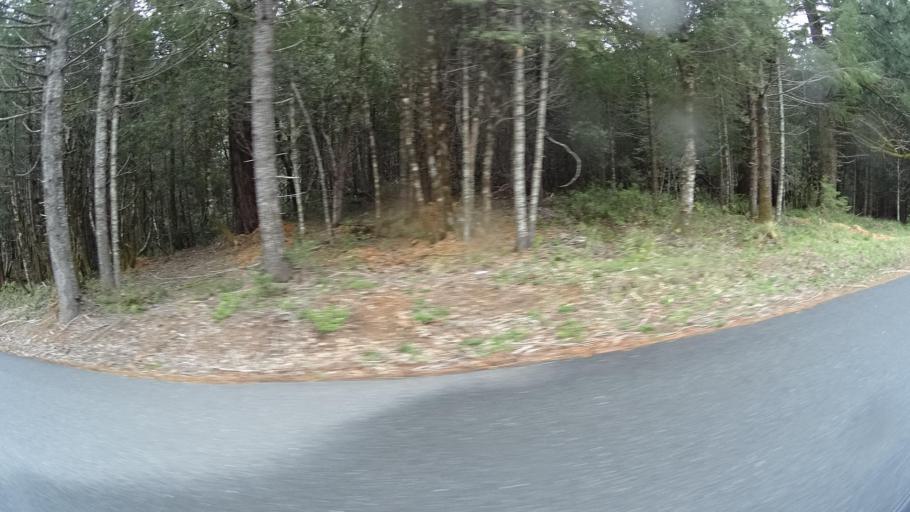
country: US
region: California
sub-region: Humboldt County
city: Willow Creek
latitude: 41.2015
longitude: -123.8018
